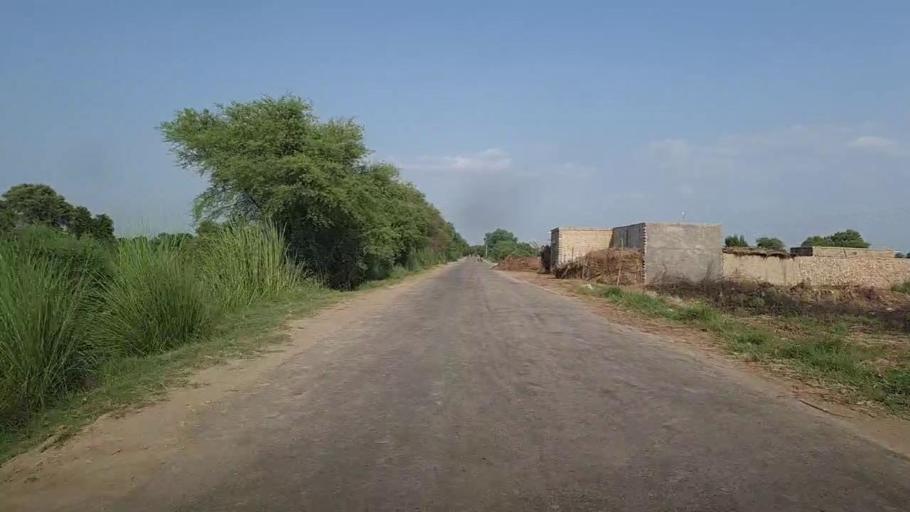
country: PK
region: Sindh
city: Khairpur
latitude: 28.0759
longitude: 69.8066
